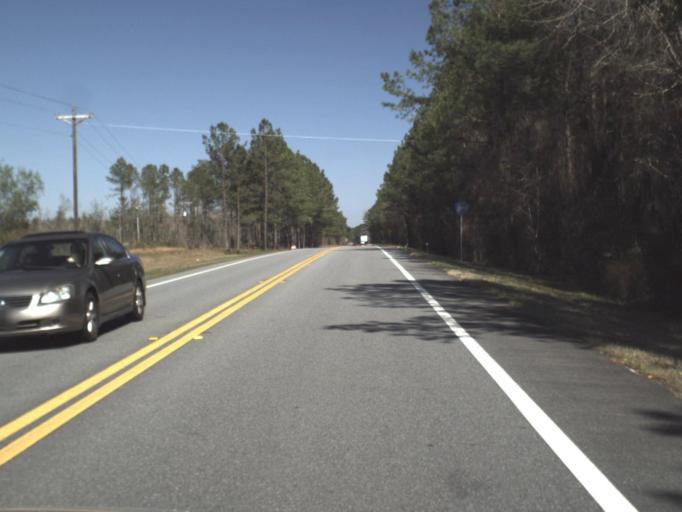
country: US
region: Florida
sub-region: Gulf County
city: Wewahitchka
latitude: 30.2824
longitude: -85.1513
